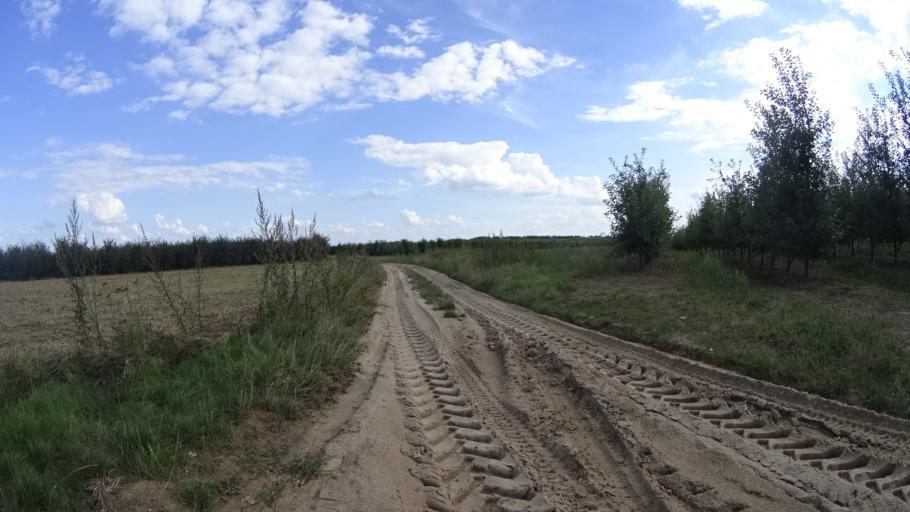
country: PL
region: Masovian Voivodeship
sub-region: Powiat bialobrzeski
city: Wysmierzyce
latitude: 51.6668
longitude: 20.8109
